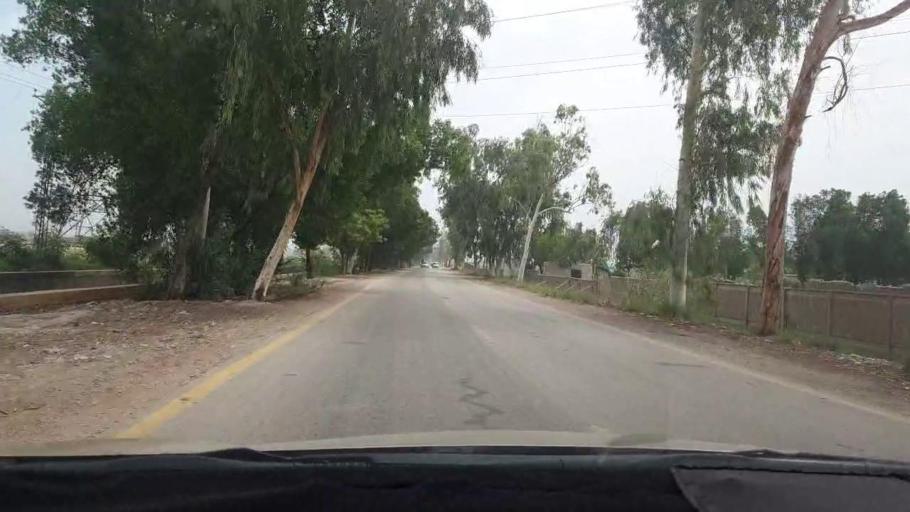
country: PK
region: Sindh
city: Naudero
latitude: 27.6647
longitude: 68.3468
